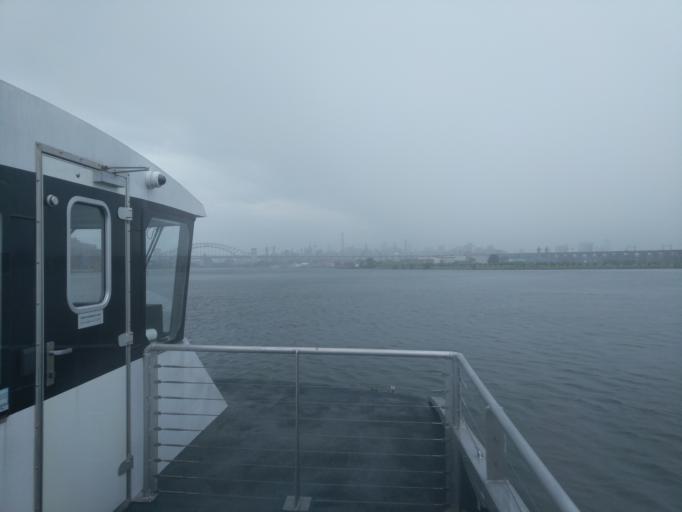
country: US
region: New York
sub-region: New York County
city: Manhattan
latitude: 40.7955
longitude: -73.9083
